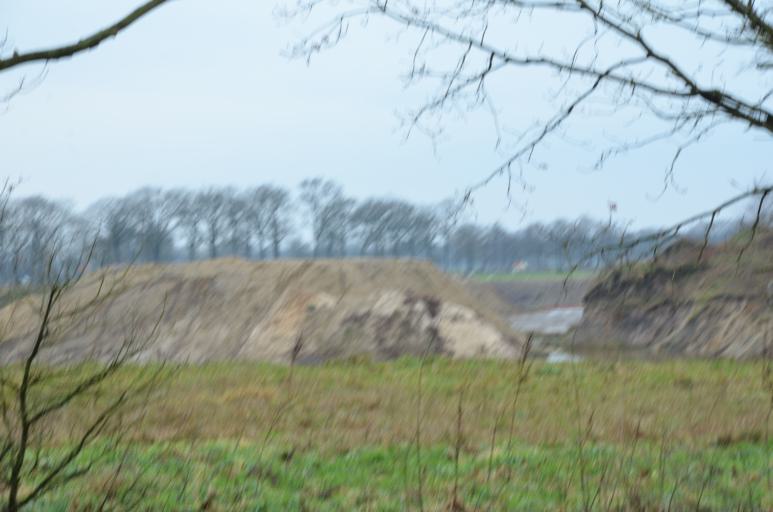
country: BE
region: Flanders
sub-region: Provincie Antwerpen
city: Oostmalle
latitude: 51.3212
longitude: 4.6965
